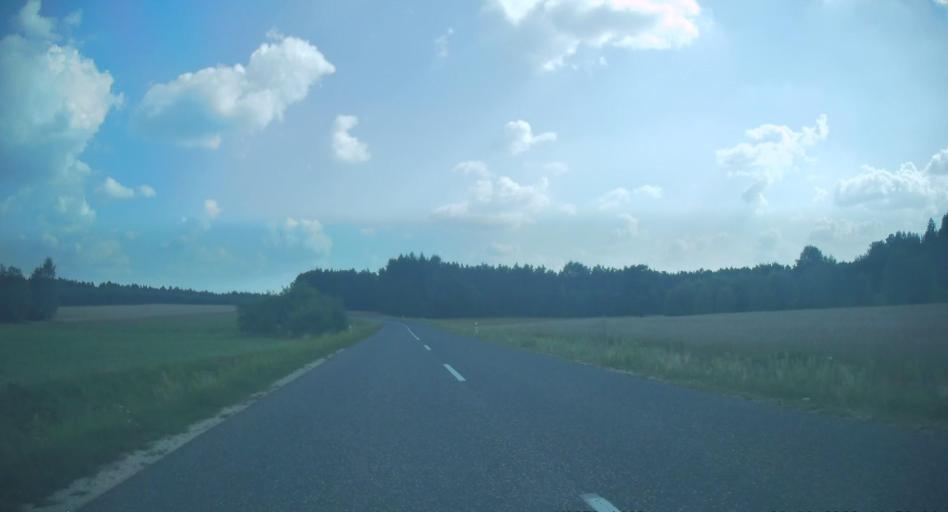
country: PL
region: Swietokrzyskie
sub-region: Powiat kielecki
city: Lopuszno
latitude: 50.9025
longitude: 20.2474
